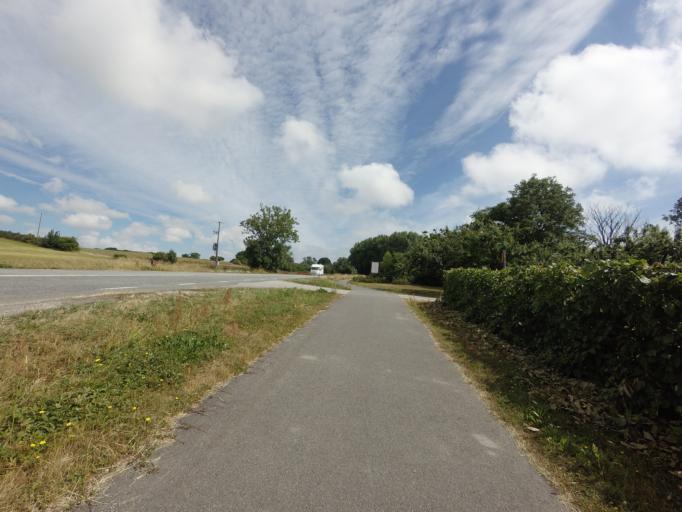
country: SE
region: Skane
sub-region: Simrishamns Kommun
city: Simrishamn
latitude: 55.4980
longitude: 14.3185
